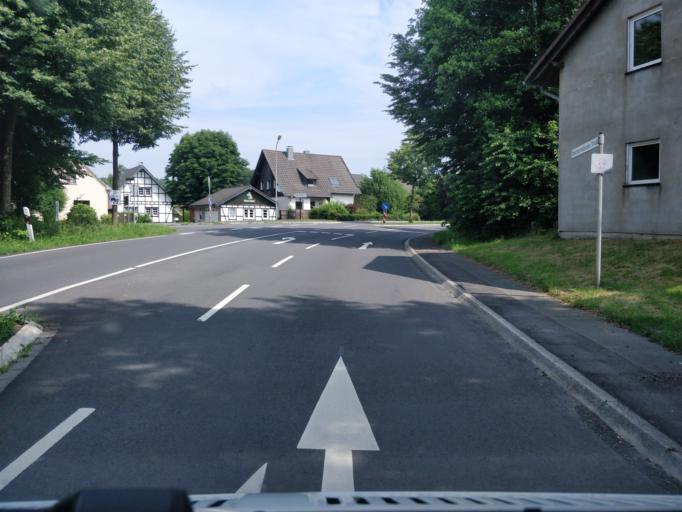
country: DE
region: North Rhine-Westphalia
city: Wiehl
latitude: 50.9324
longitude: 7.5750
